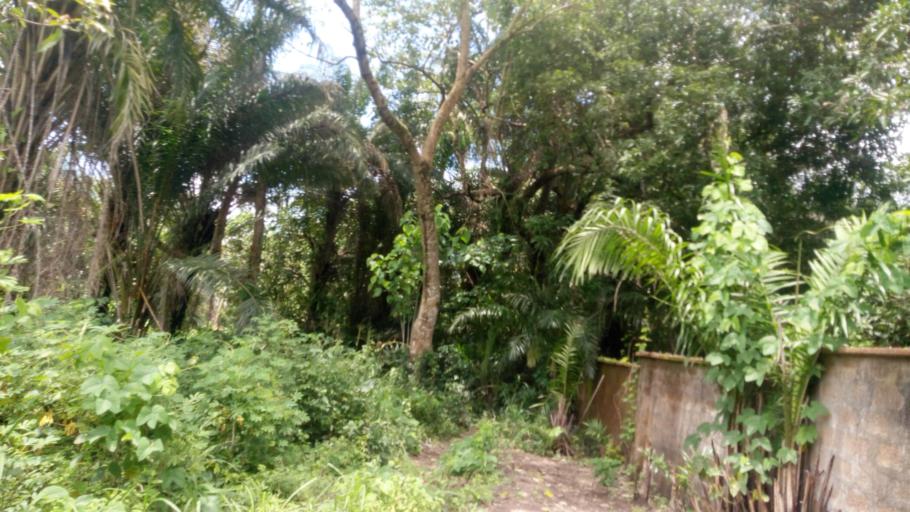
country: SL
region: Northern Province
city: Magburaka
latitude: 8.7130
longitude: -11.9509
